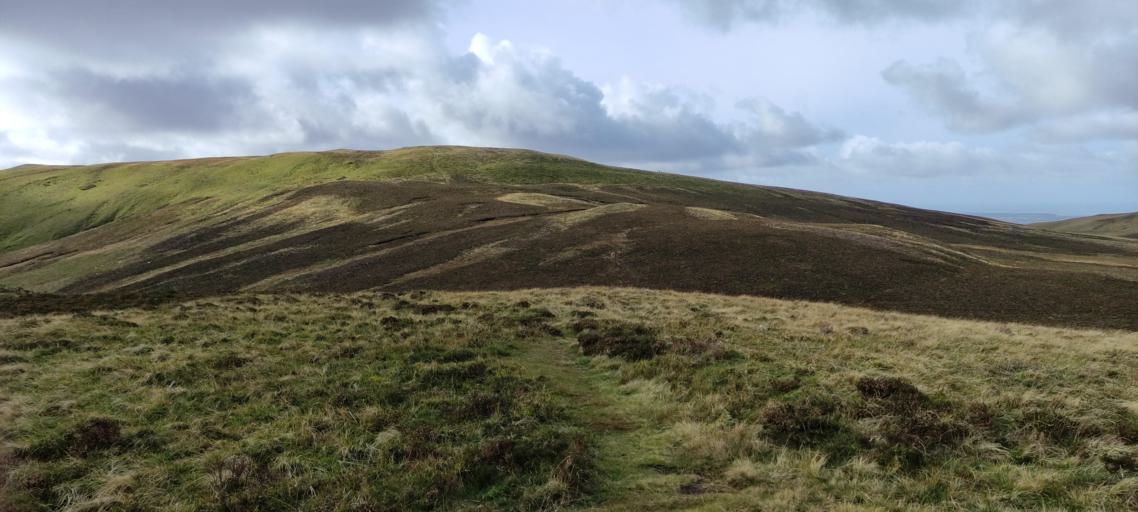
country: GB
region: England
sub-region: Cumbria
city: Cockermouth
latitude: 54.5579
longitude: -3.3615
